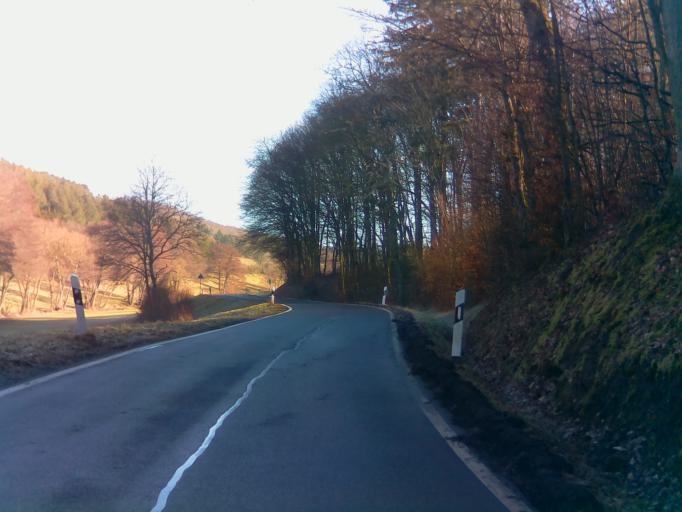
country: DE
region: Rheinland-Pfalz
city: Auen
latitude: 49.8338
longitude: 7.6097
